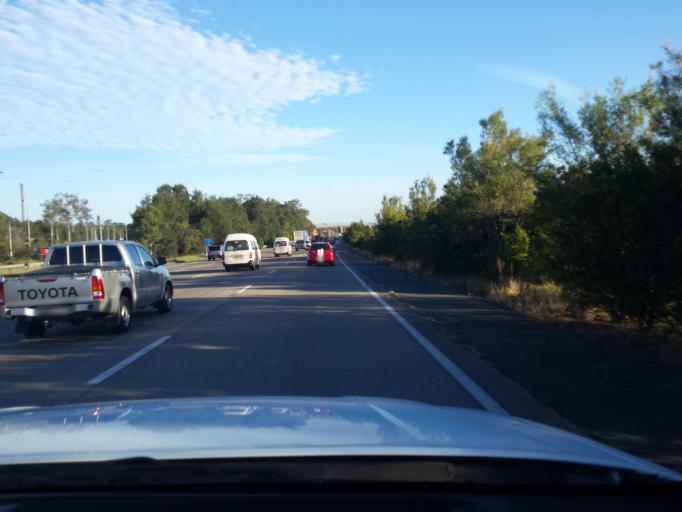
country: AU
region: Queensland
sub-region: Gold Coast
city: Oxenford
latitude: -27.8524
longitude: 153.3078
